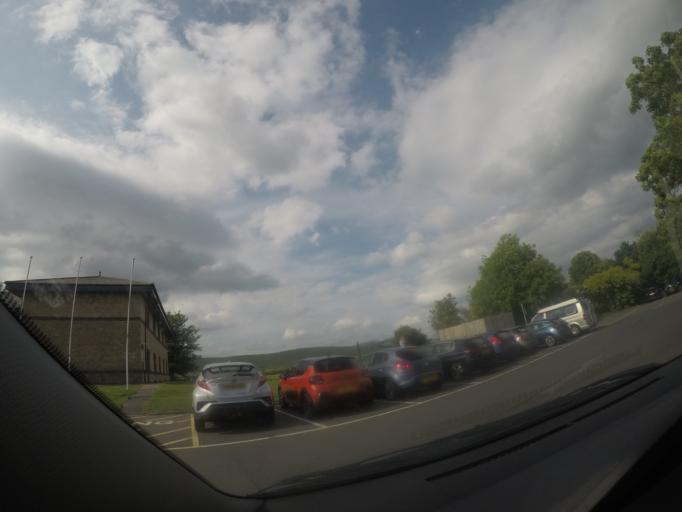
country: GB
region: Scotland
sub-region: South Lanarkshire
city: Douglas
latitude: 55.5077
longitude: -3.6950
